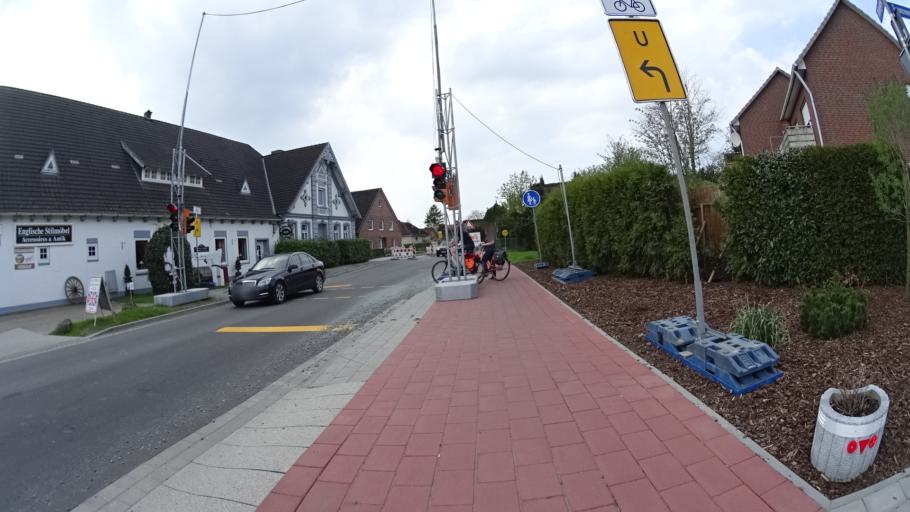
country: DE
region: Lower Saxony
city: Jork
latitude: 53.5254
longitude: 9.7093
